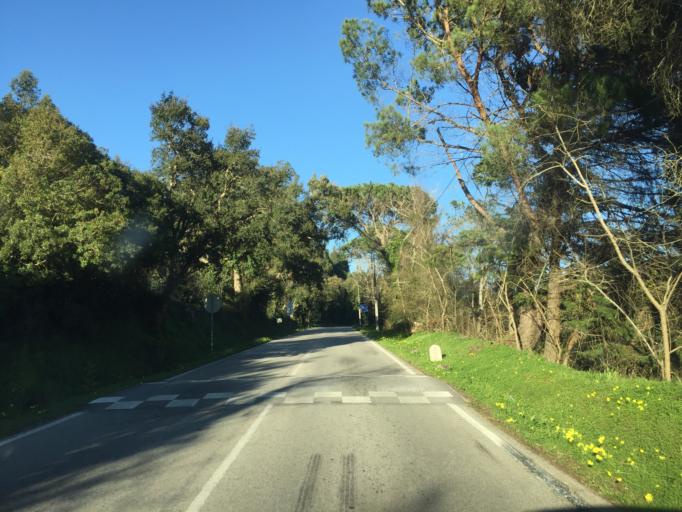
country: PT
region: Coimbra
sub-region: Figueira da Foz
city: Alhadas
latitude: 40.1693
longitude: -8.8058
